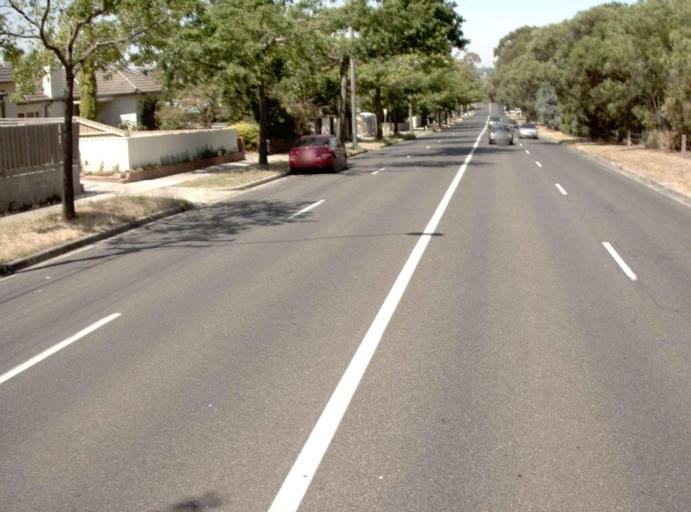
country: AU
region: Victoria
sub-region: Whitehorse
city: Box Hill South
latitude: -37.8397
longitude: 145.1108
